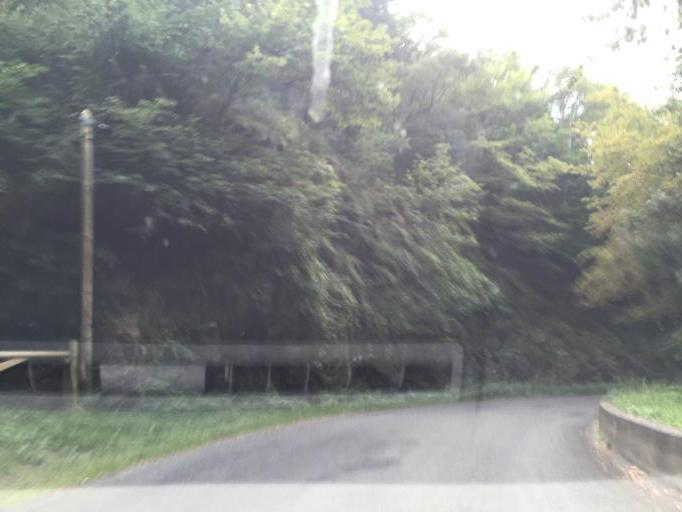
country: FR
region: Rhone-Alpes
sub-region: Departement de la Loire
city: Saint-Jean-Bonnefonds
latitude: 45.4168
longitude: 4.4466
